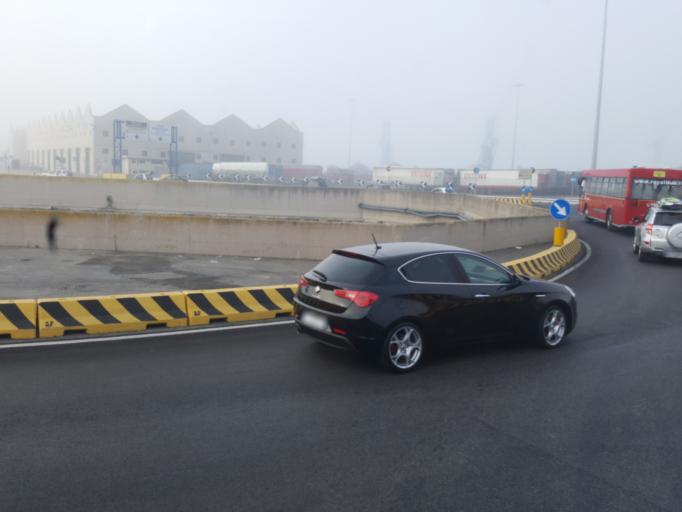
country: IT
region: Latium
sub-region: Citta metropolitana di Roma Capitale
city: Civitavecchia
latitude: 42.1040
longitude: 11.7805
